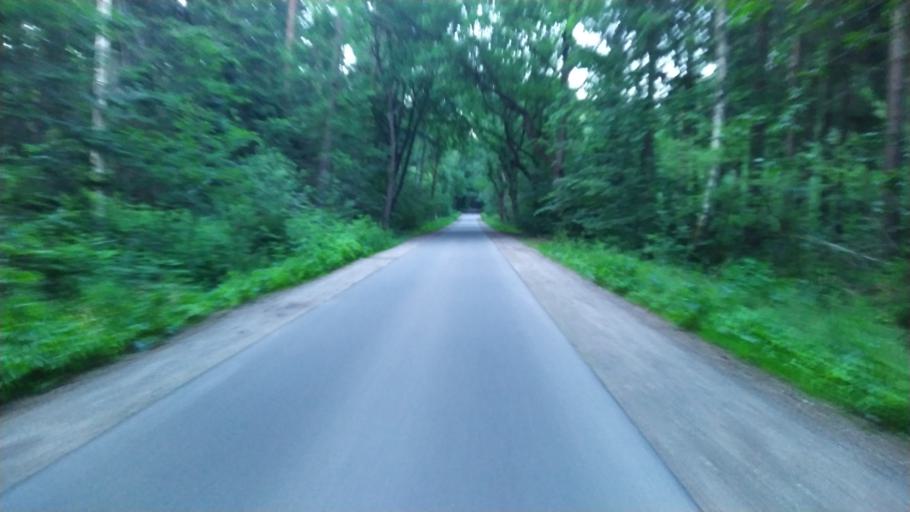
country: DE
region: Lower Saxony
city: Deinstedt
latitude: 53.4966
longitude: 9.2482
